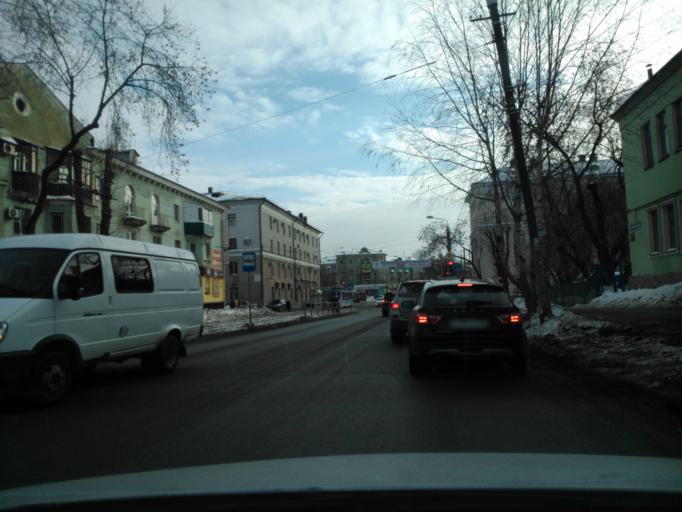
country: RU
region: Perm
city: Perm
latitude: 57.9949
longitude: 56.2465
